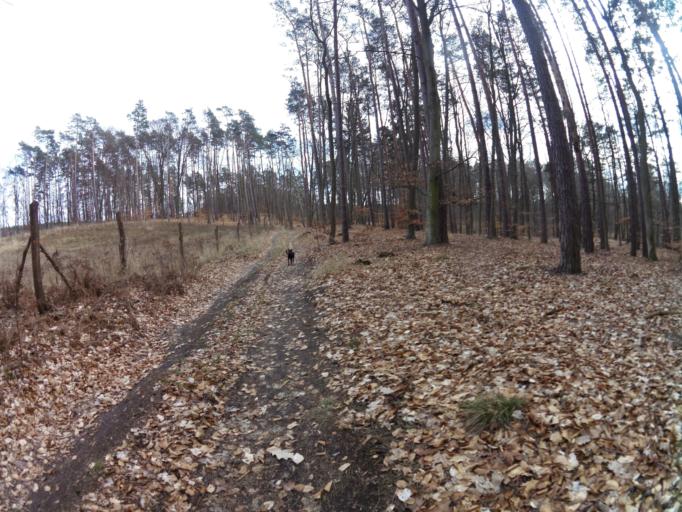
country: PL
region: Lubusz
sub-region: Powiat gorzowski
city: Lubiszyn
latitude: 52.7842
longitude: 14.8432
